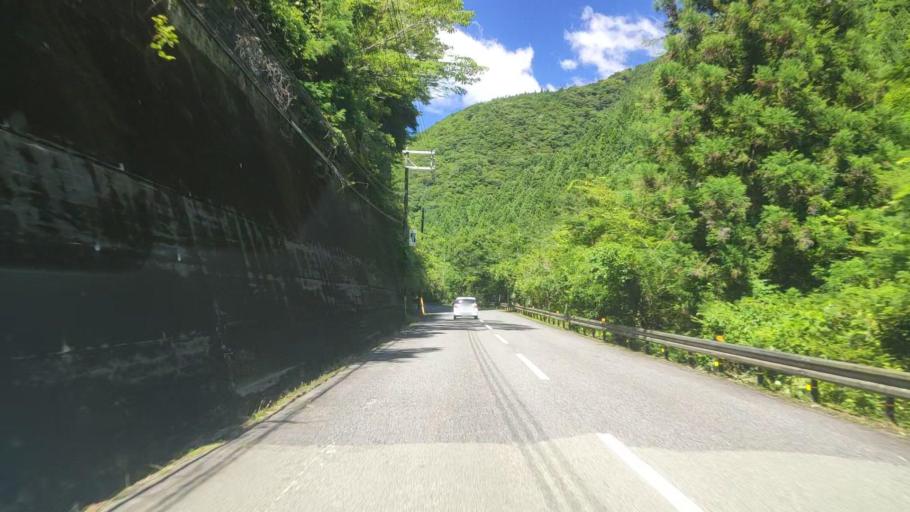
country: JP
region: Mie
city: Owase
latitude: 34.1716
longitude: 136.0020
